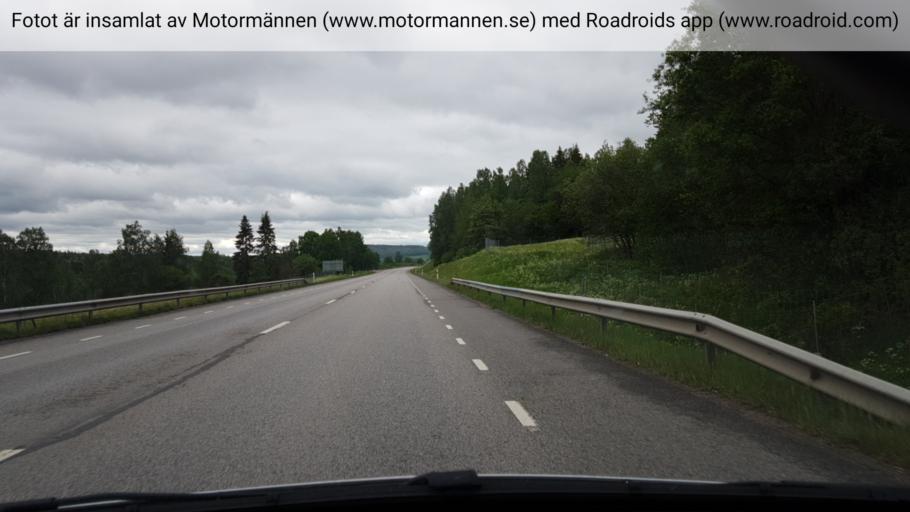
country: SE
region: Joenkoeping
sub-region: Tranas Kommun
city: Tranas
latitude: 58.0153
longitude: 14.9367
